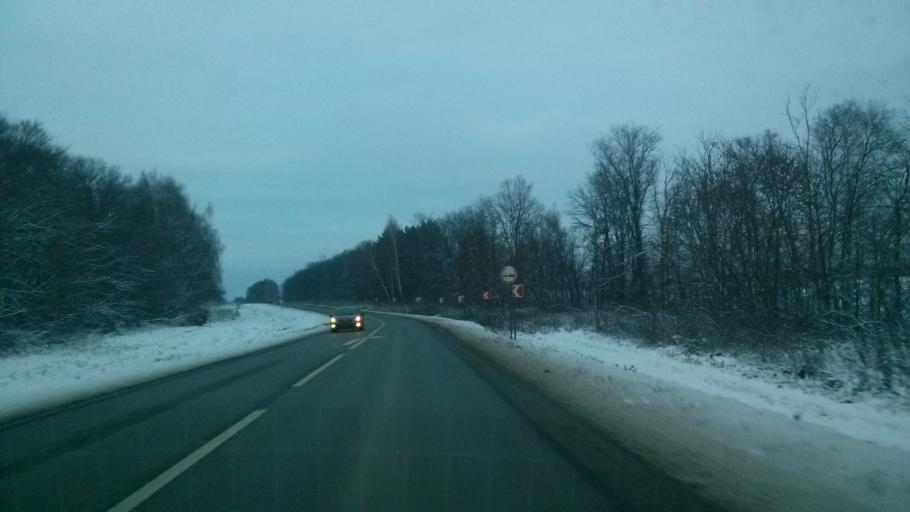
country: RU
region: Nizjnij Novgorod
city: Bogorodsk
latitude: 56.0509
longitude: 43.4026
